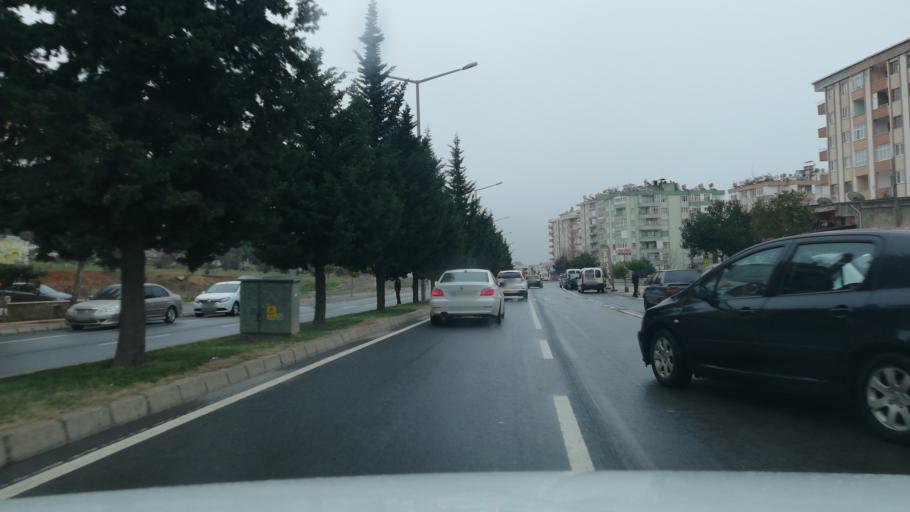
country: TR
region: Kahramanmaras
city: Kahramanmaras
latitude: 37.5911
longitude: 36.8834
